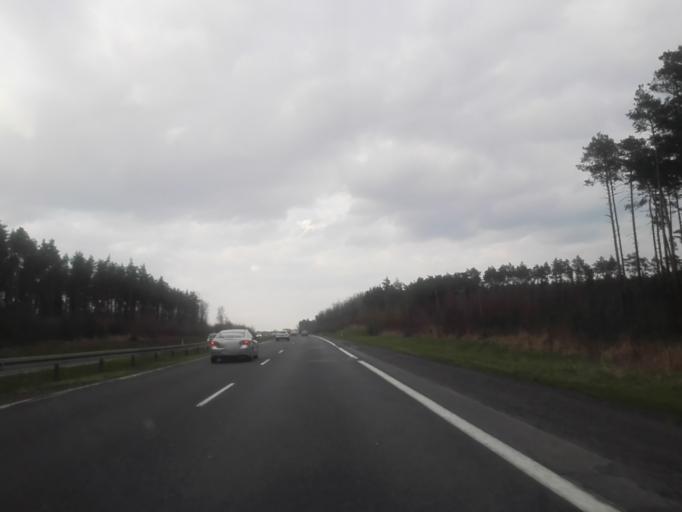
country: PL
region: Lodz Voivodeship
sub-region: Powiat radomszczanski
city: Gomunice
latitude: 51.1656
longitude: 19.4579
